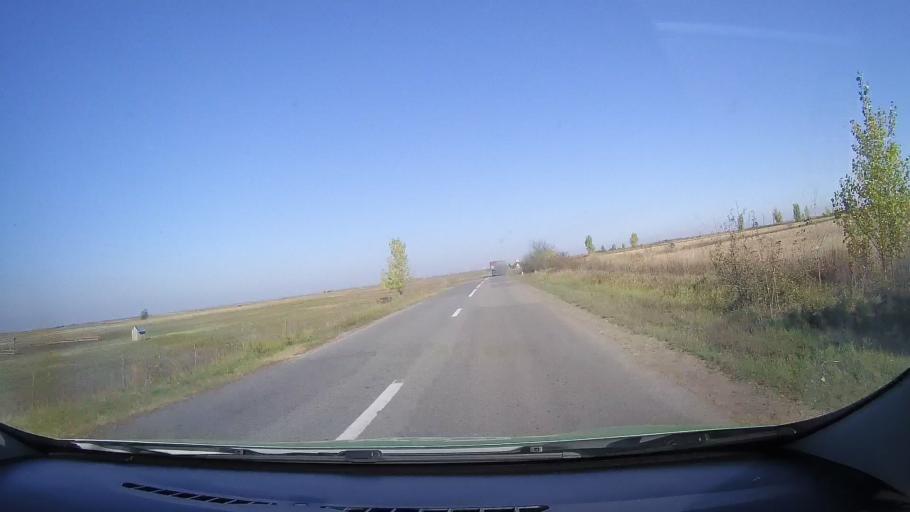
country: RO
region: Satu Mare
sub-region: Comuna Cauas
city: Cauas
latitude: 47.5339
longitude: 22.5656
